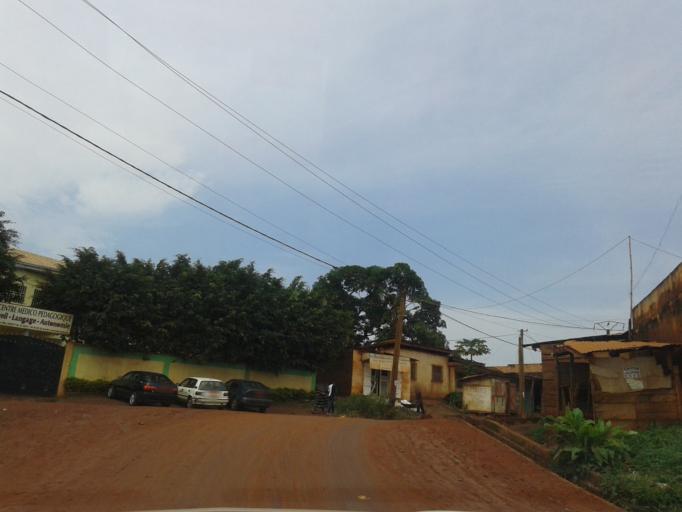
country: CM
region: Centre
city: Yaounde
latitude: 3.9253
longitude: 11.5161
